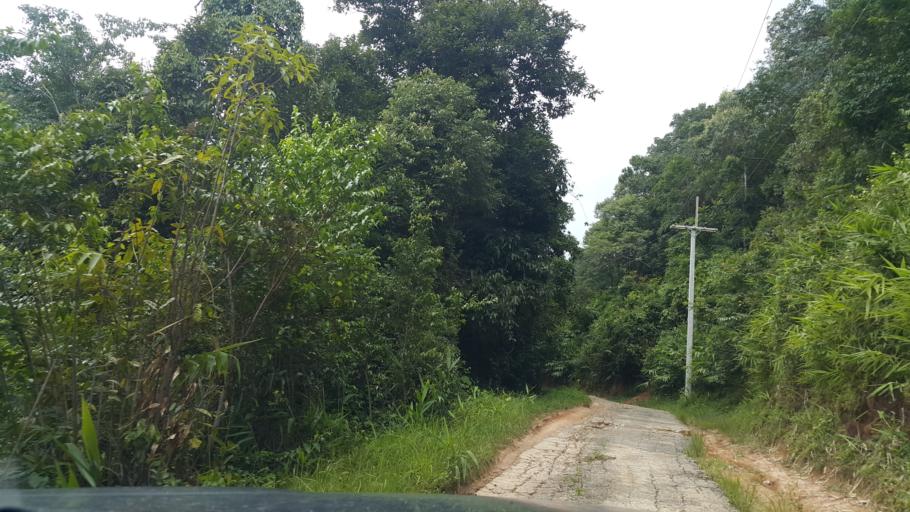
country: TH
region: Lampang
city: Wang Nuea
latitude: 19.1024
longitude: 99.3672
